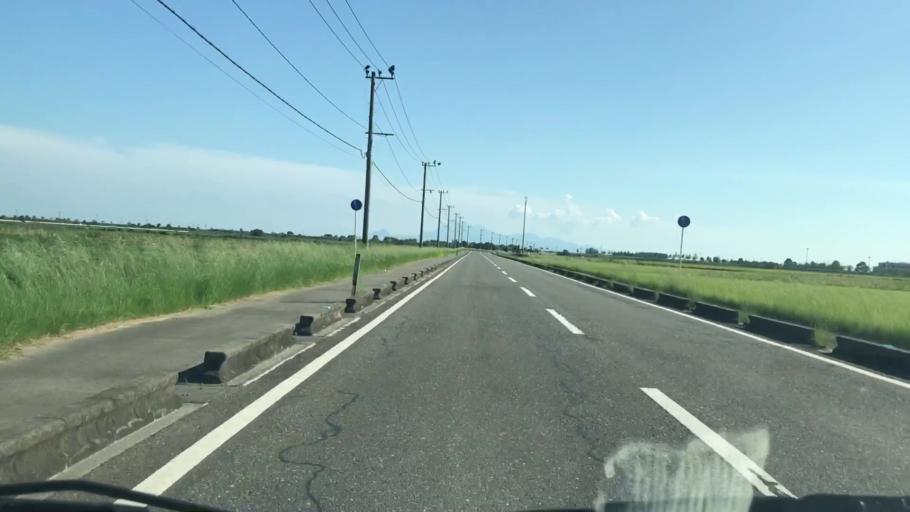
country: JP
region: Saga Prefecture
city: Okawa
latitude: 33.1618
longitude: 130.3087
